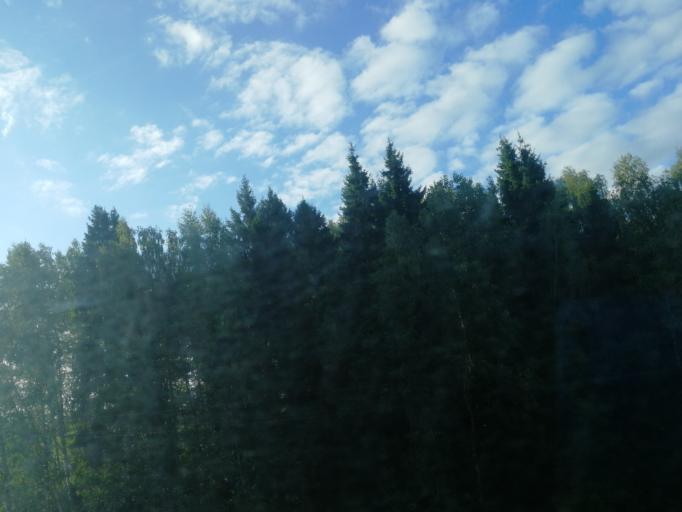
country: RU
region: Kaluga
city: Kaluga
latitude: 54.4353
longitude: 36.3517
